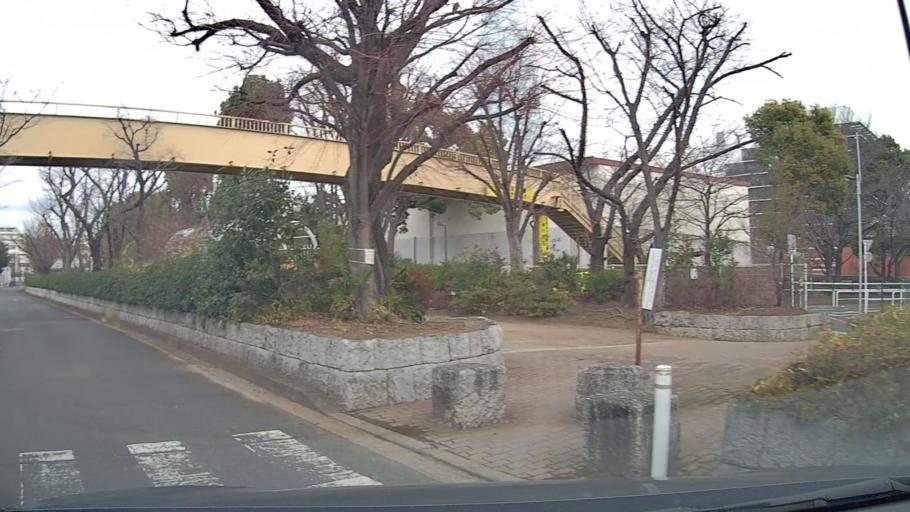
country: JP
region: Saitama
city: Shimotoda
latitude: 35.7913
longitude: 139.6648
